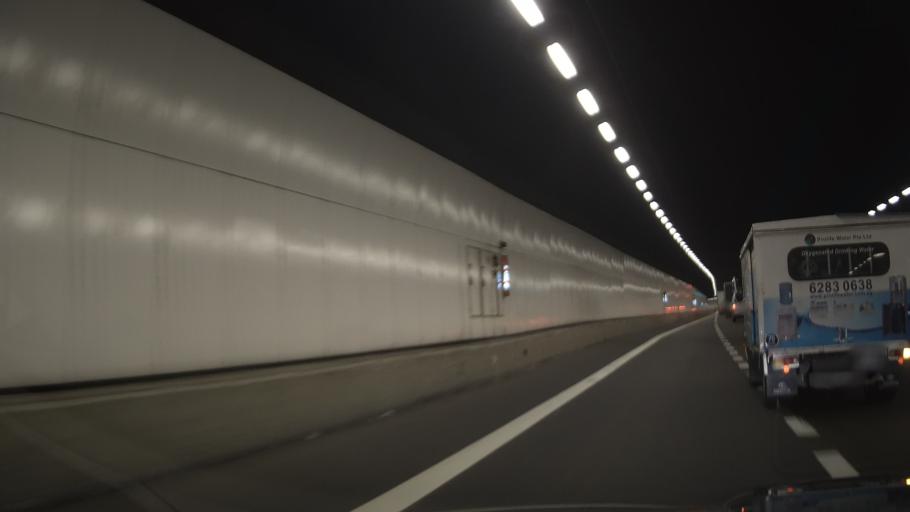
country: SG
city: Singapore
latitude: 1.3195
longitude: 103.8850
